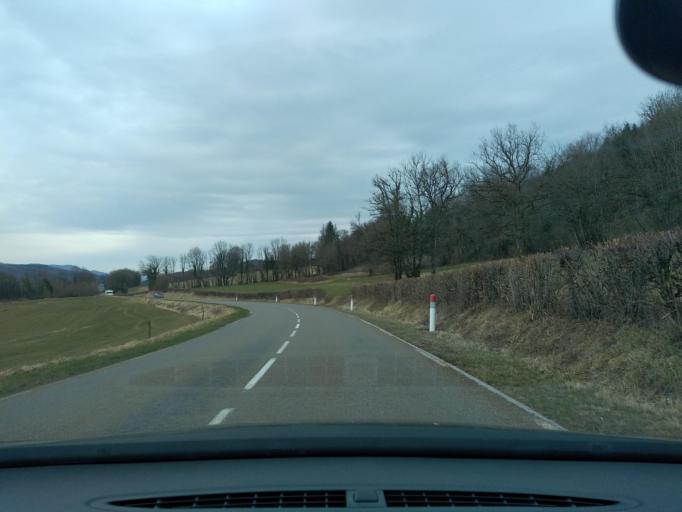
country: FR
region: Franche-Comte
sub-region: Departement du Jura
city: Orgelet
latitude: 46.5012
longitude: 5.5877
